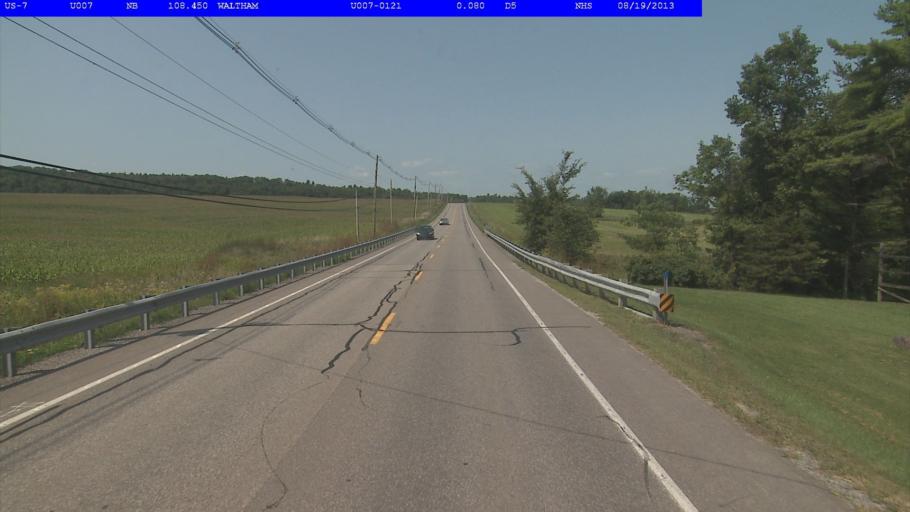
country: US
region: Vermont
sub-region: Addison County
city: Vergennes
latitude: 44.1485
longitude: -73.2112
